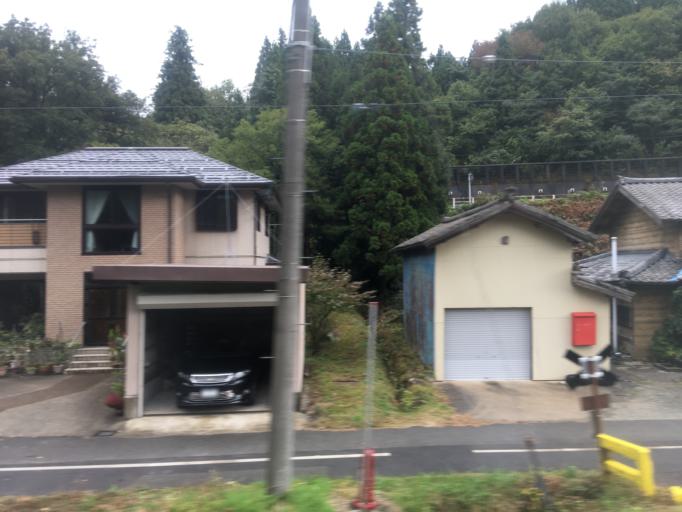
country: JP
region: Niigata
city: Murakami
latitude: 38.0777
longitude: 139.6614
